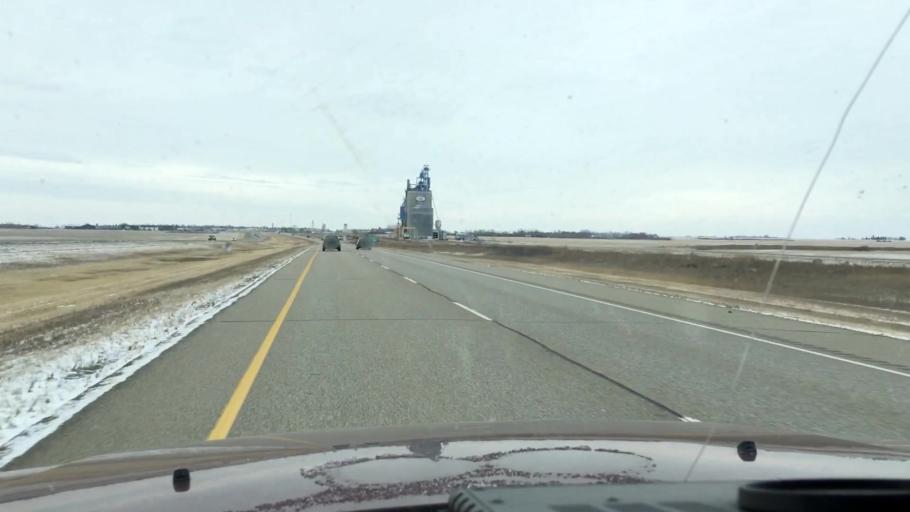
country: CA
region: Saskatchewan
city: Watrous
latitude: 51.2853
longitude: -106.0224
